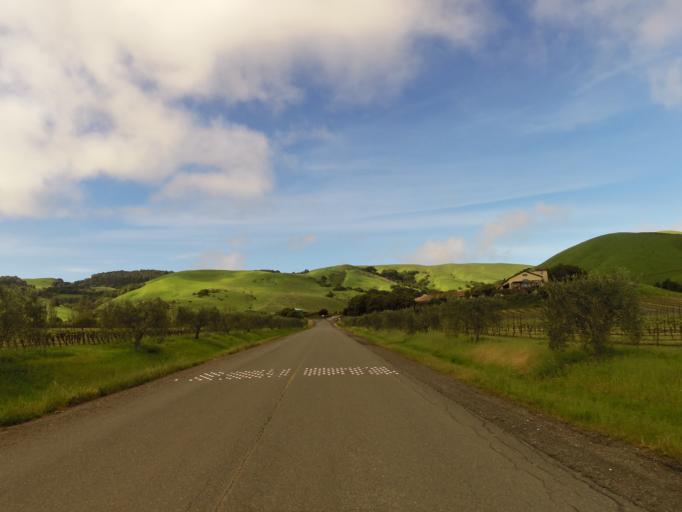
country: US
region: California
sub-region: Sonoma County
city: Temelec
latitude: 38.2240
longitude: -122.4684
